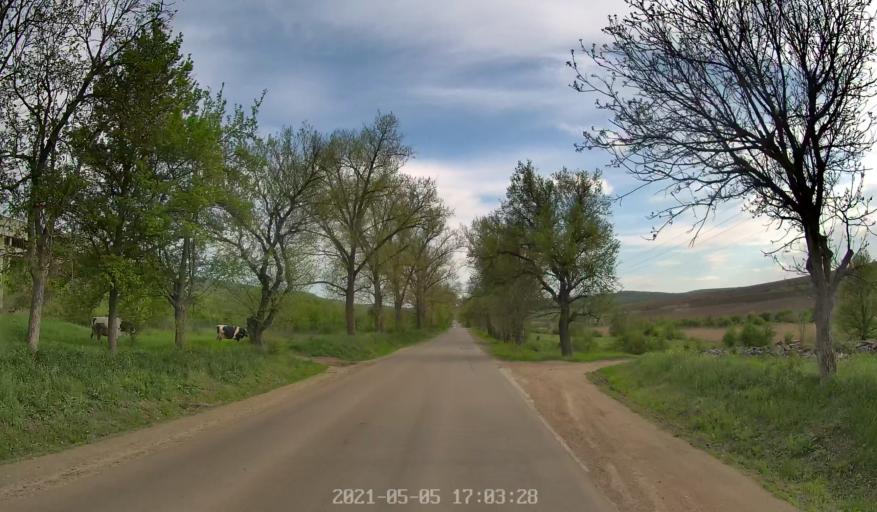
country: MD
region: Chisinau
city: Vadul lui Voda
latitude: 47.0512
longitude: 29.1334
